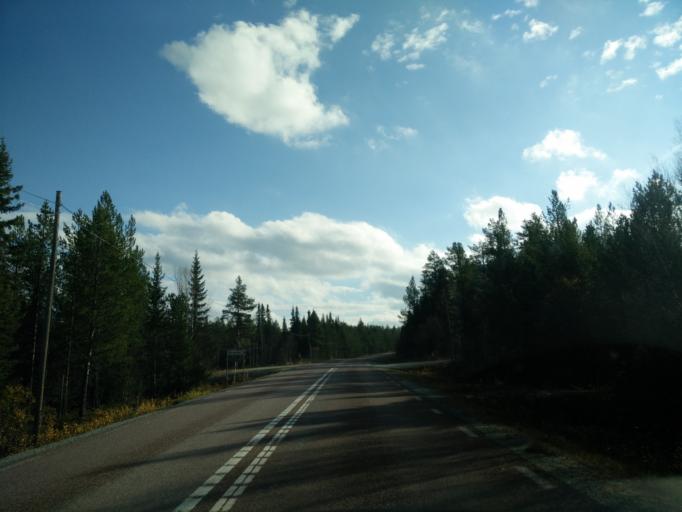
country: NO
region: Hedmark
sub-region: Engerdal
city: Engerdal
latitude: 62.5037
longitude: 12.6217
